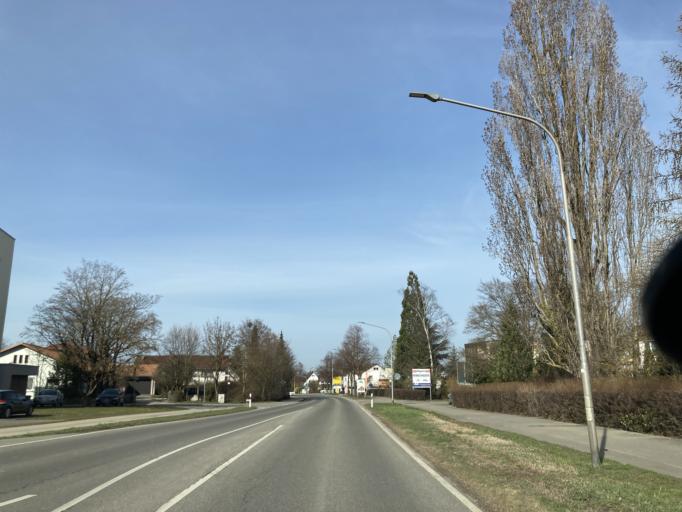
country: DE
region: Baden-Wuerttemberg
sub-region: Tuebingen Region
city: Mossingen
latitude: 48.4092
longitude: 9.0721
